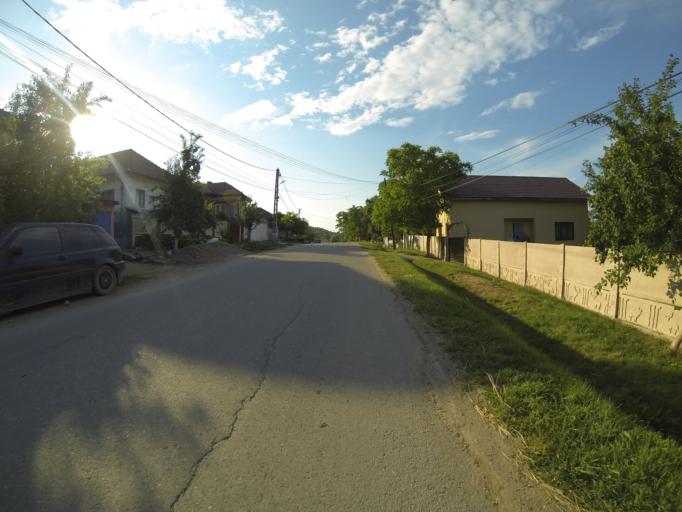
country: RO
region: Dolj
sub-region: Comuna Tuglui
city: Tuglui
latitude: 44.1982
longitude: 23.8022
